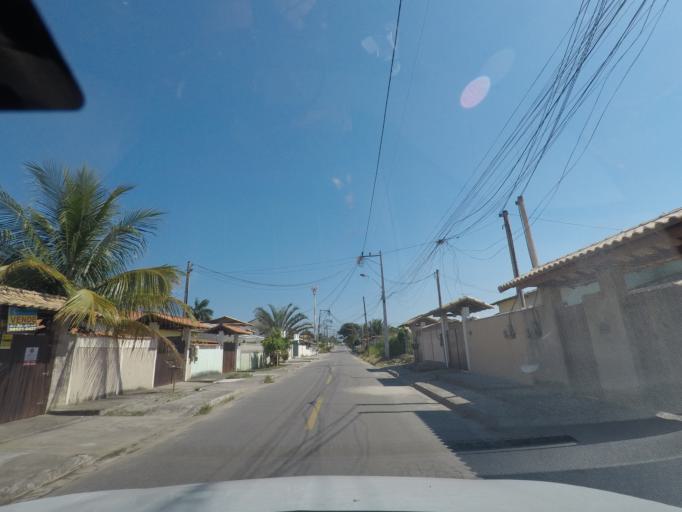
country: BR
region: Rio de Janeiro
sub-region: Niteroi
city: Niteroi
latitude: -22.9609
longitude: -42.9720
